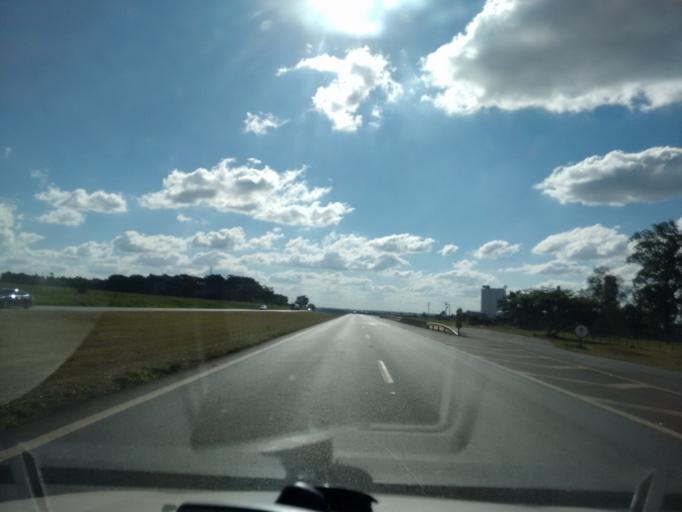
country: BR
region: Sao Paulo
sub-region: Araraquara
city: Araraquara
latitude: -21.8250
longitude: -48.1693
